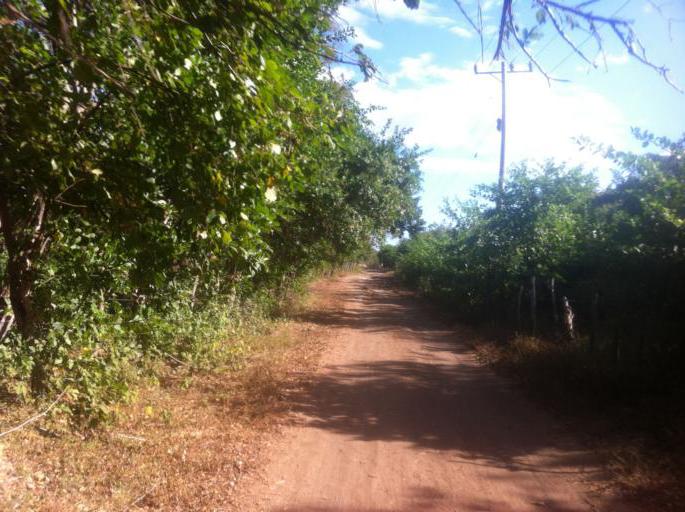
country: NI
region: Managua
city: Carlos Fonseca Amador
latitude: 11.9159
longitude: -86.5980
